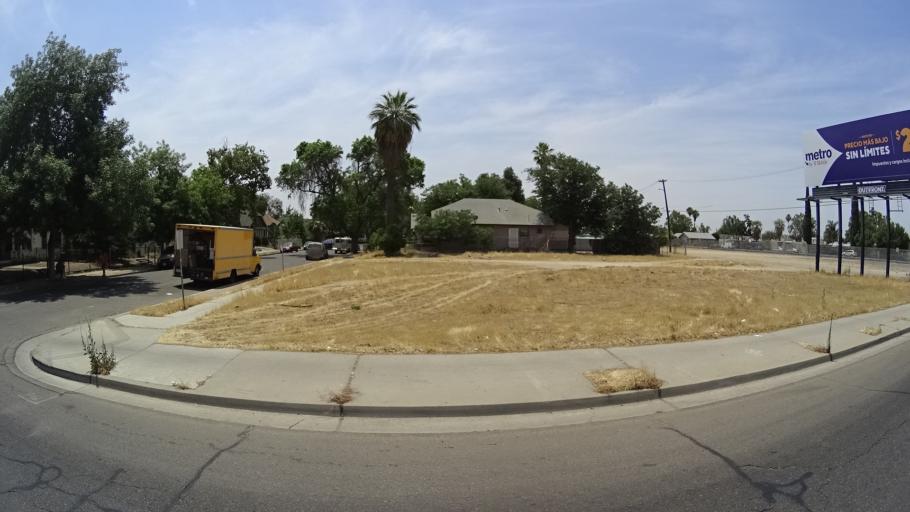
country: US
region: California
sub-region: Fresno County
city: Fresno
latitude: 36.7503
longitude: -119.7861
